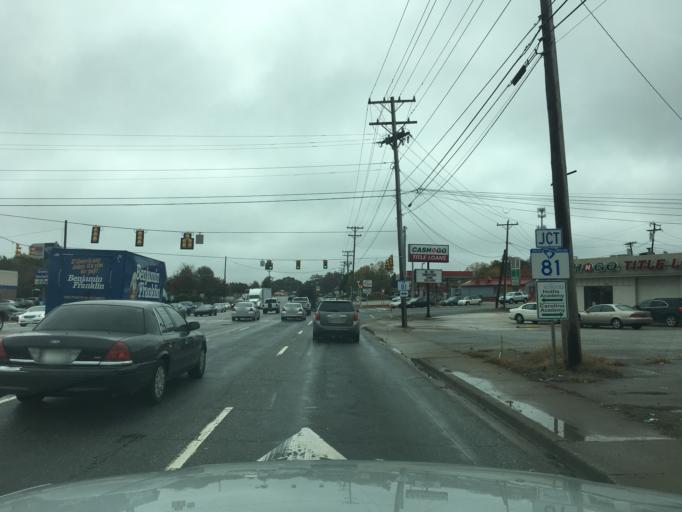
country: US
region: South Carolina
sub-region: Greenville County
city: Welcome
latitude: 34.8156
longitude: -82.4417
